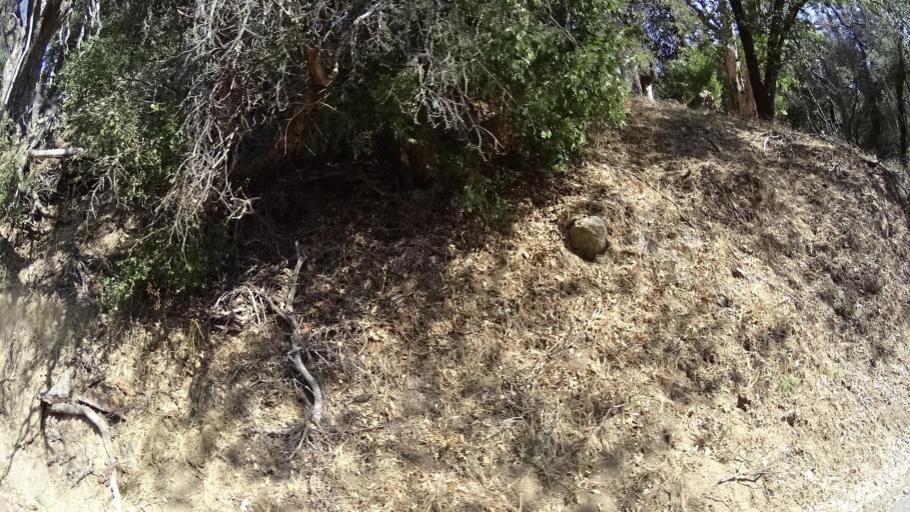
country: US
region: California
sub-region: San Diego County
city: Julian
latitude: 33.1277
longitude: -116.6013
